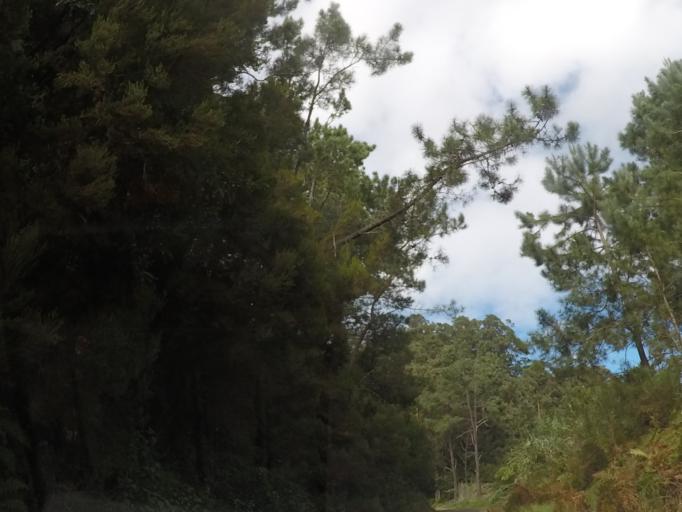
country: PT
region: Madeira
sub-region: Sao Vicente
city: Sao Vicente
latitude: 32.7798
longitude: -17.0490
